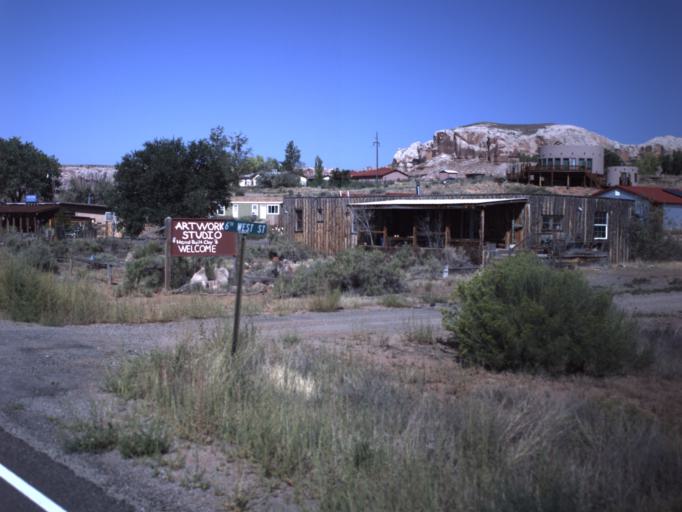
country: US
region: Utah
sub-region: San Juan County
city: Blanding
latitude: 37.2815
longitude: -109.5696
